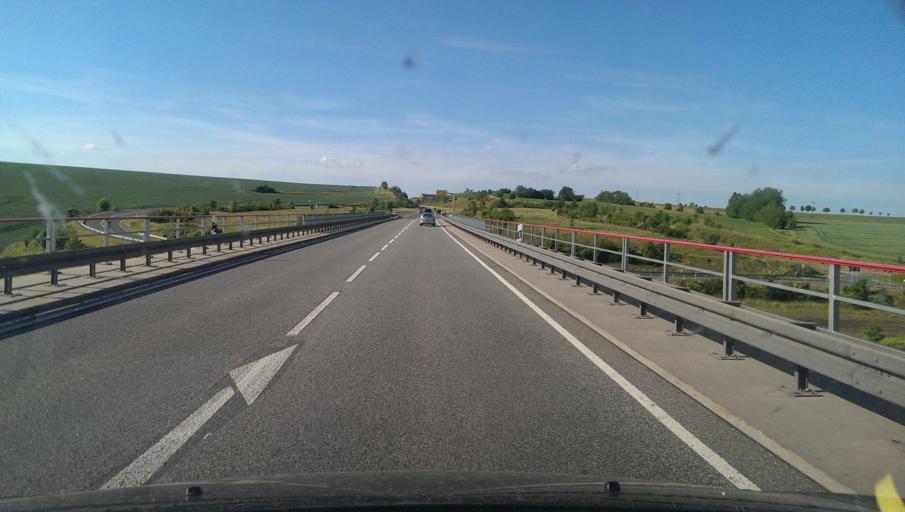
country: DE
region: Thuringia
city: Schwaara
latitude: 50.9178
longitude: 12.1339
